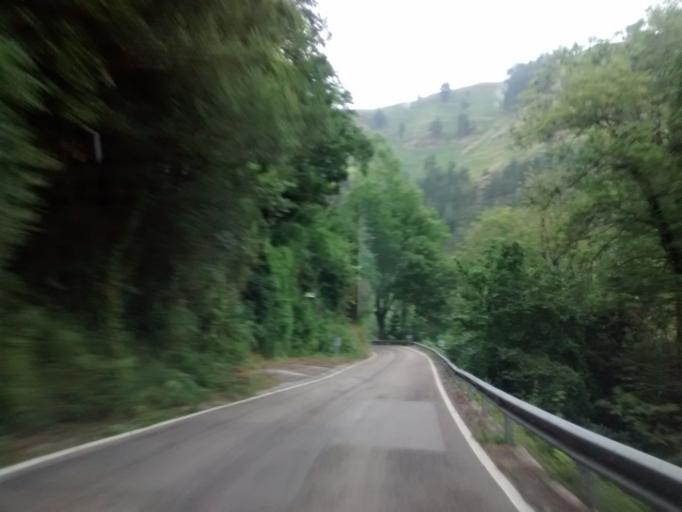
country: ES
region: Cantabria
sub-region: Provincia de Cantabria
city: Vega de Pas
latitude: 43.1670
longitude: -3.8352
